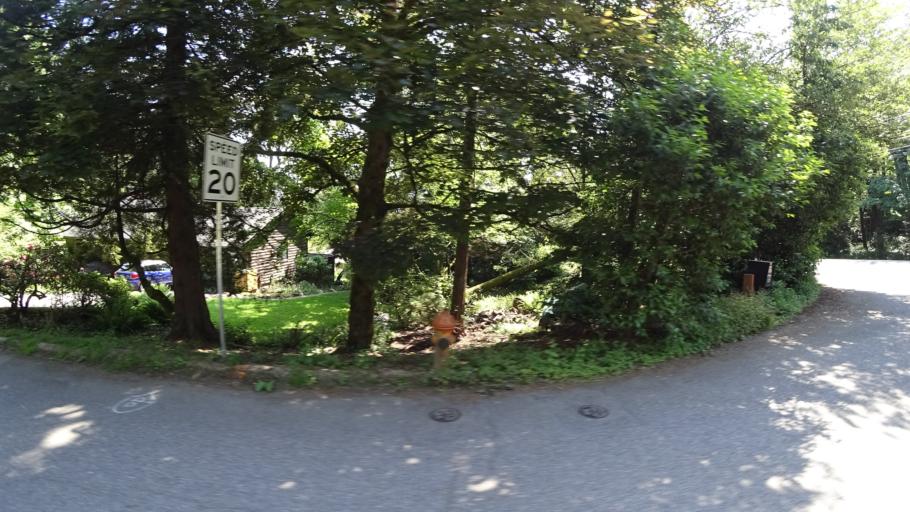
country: US
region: Oregon
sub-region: Washington County
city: West Haven-Sylvan
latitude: 45.5201
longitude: -122.7276
